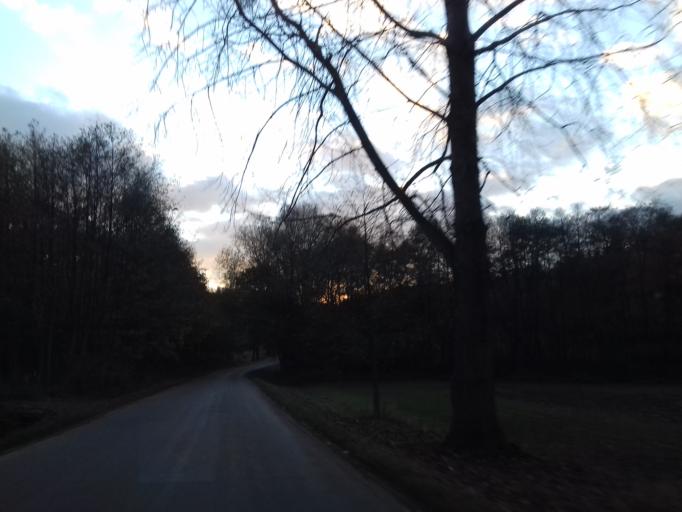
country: CZ
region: Pardubicky
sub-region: Okres Chrudim
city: Hlinsko
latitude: 49.7941
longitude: 15.9499
